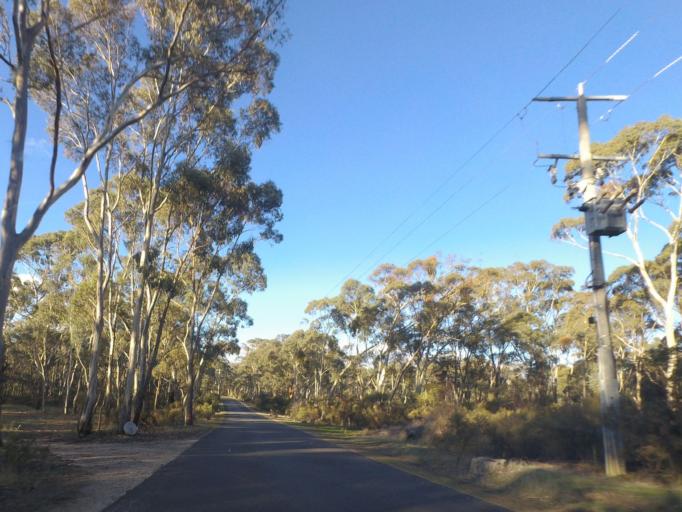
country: AU
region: Victoria
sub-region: Mount Alexander
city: Castlemaine
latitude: -37.1427
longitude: 144.1947
